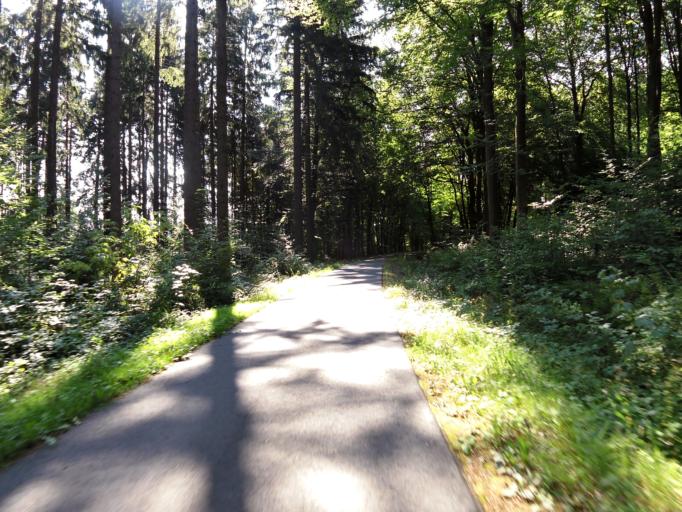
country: DE
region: Baden-Wuerttemberg
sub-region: Karlsruhe Region
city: Mudau
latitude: 49.5120
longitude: 9.2132
